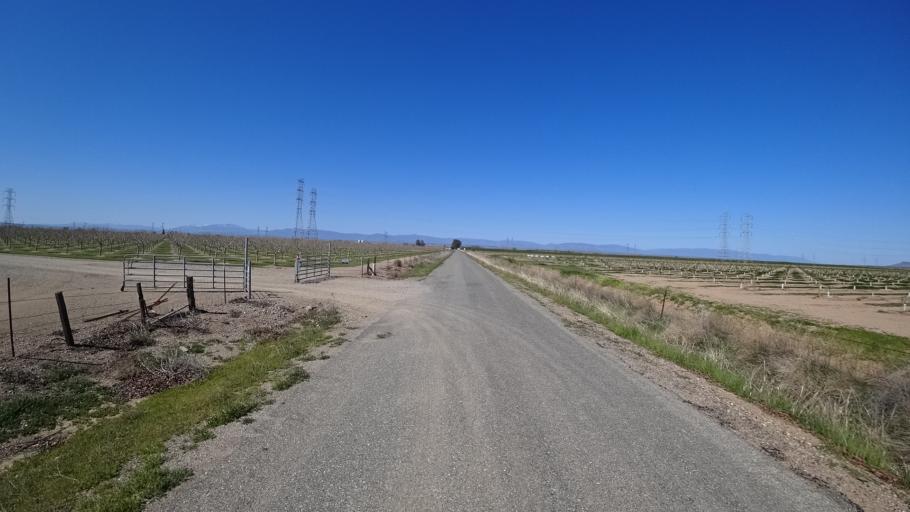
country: US
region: California
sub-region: Glenn County
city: Orland
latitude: 39.6539
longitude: -122.2625
